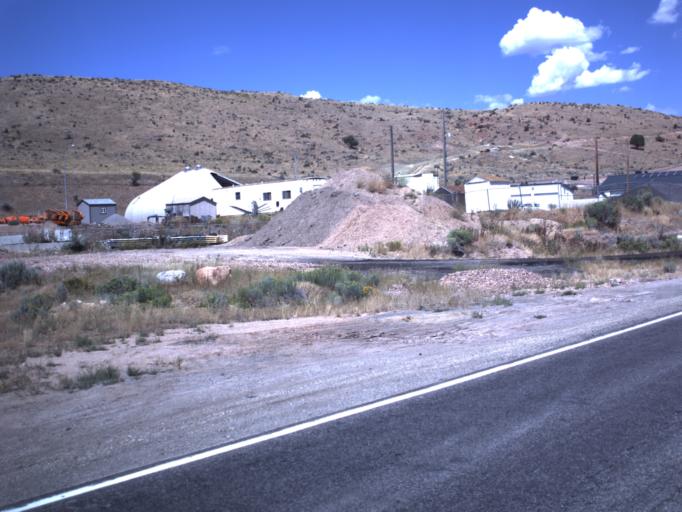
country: US
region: Utah
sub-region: Summit County
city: Coalville
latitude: 40.8004
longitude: -111.4090
